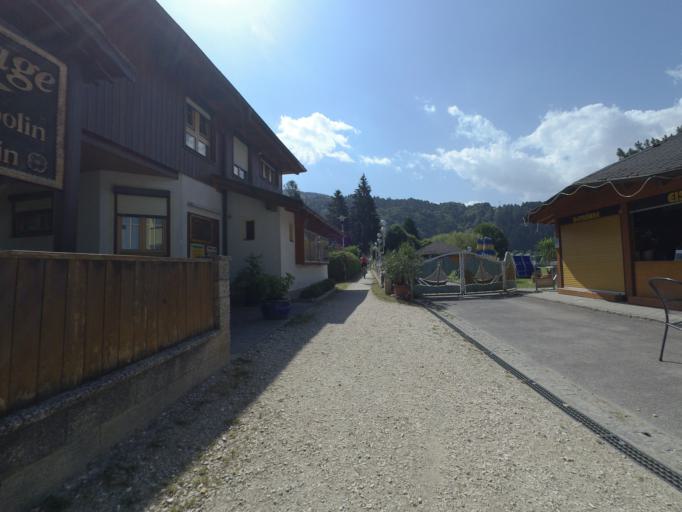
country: AT
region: Carinthia
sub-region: Politischer Bezirk Villach Land
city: Ferndorf
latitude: 46.7718
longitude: 13.6444
